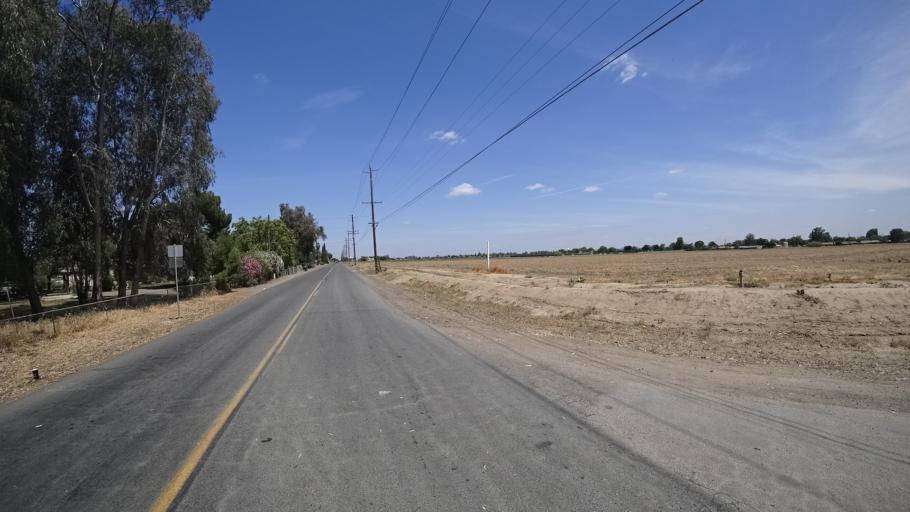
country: US
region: California
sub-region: Kings County
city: Home Garden
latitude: 36.2986
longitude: -119.6460
